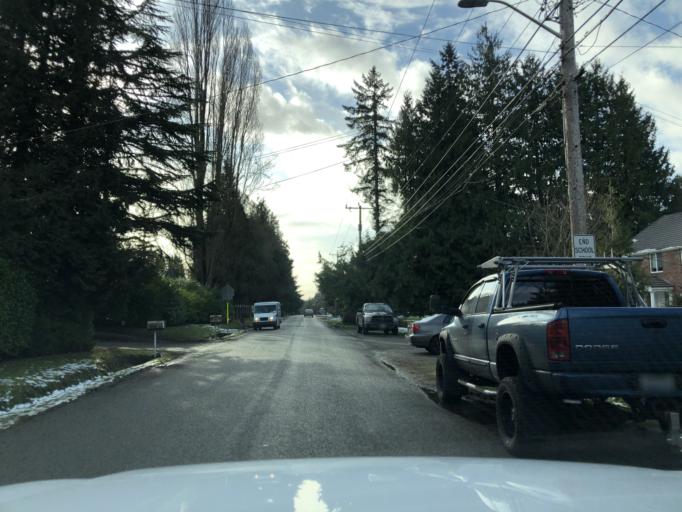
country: US
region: Washington
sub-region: King County
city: Lake Forest Park
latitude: 47.7244
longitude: -122.2864
